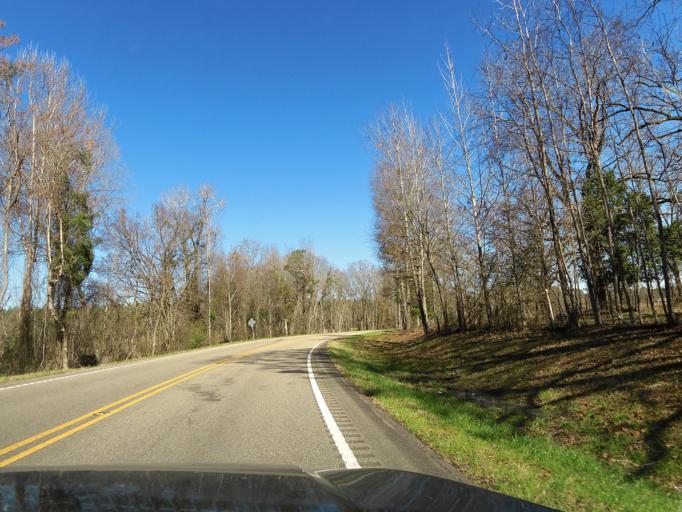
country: US
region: Alabama
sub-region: Bullock County
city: Union Springs
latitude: 32.1400
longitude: -85.7657
